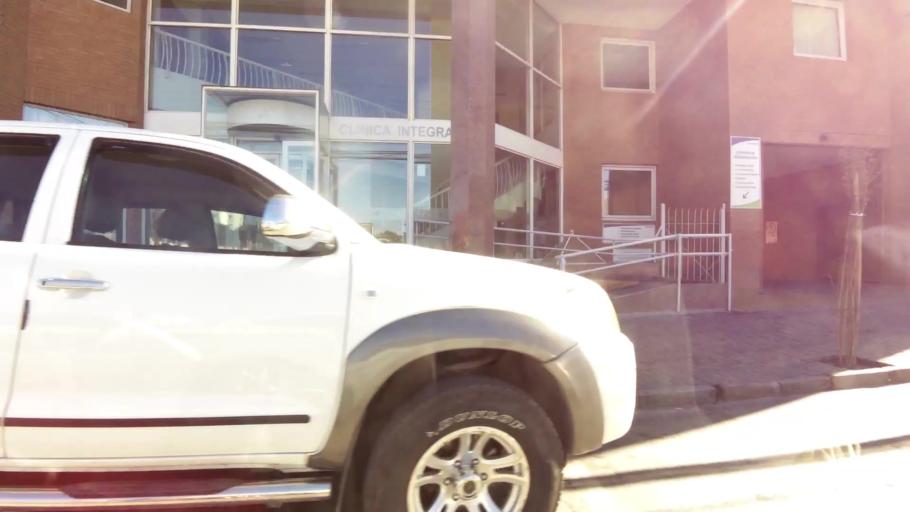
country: CL
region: O'Higgins
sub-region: Provincia de Cachapoal
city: Rancagua
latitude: -34.1664
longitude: -70.7433
